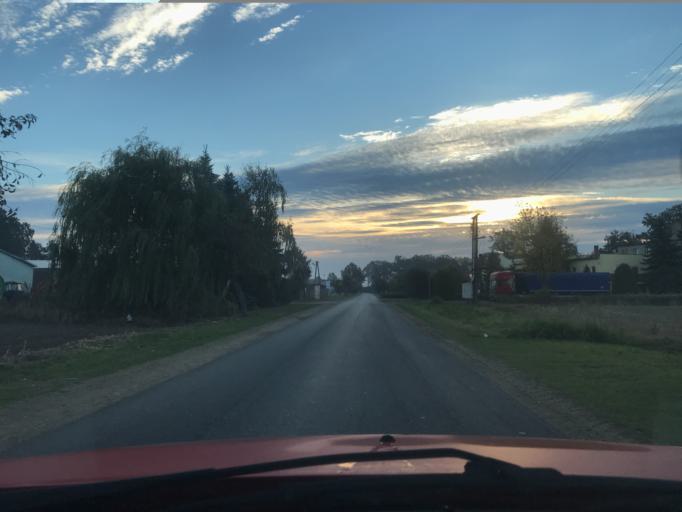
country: PL
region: Greater Poland Voivodeship
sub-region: Powiat ostrowski
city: Raszkow
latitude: 51.7193
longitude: 17.7869
